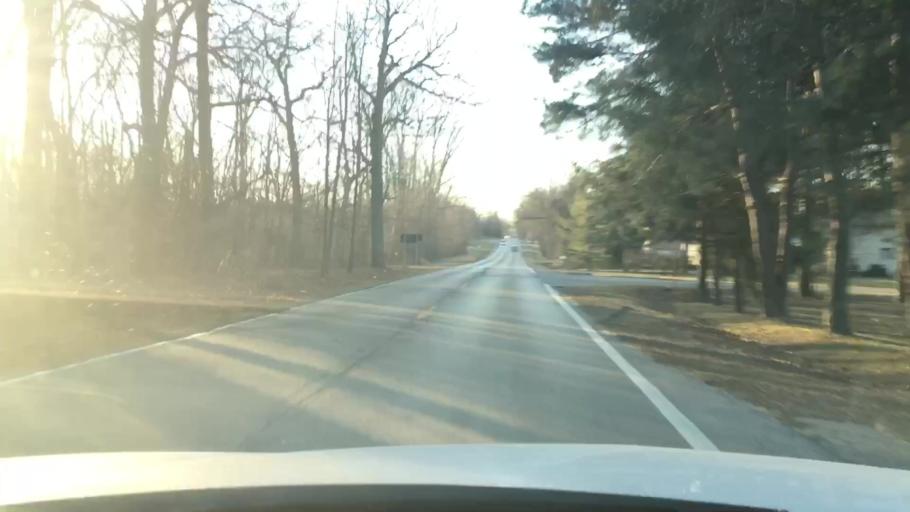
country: US
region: Michigan
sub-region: Oakland County
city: Wolverine Lake
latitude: 42.5991
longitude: -83.4346
